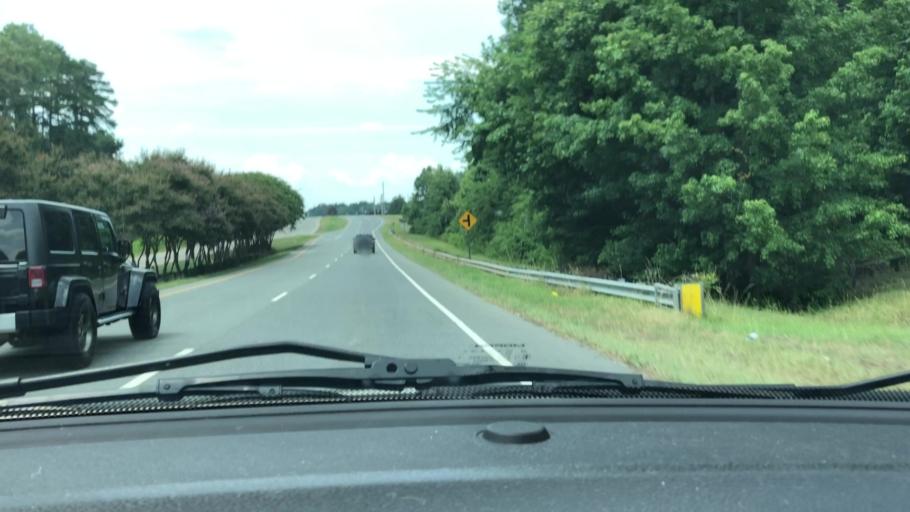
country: US
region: North Carolina
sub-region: Lee County
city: Sanford
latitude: 35.5094
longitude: -79.2108
